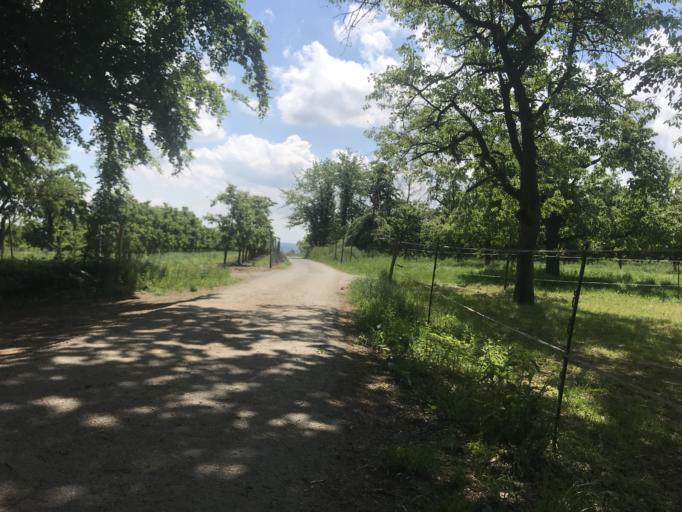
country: DE
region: Hesse
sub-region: Regierungsbezirk Darmstadt
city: Walluf
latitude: 50.0715
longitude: 8.1570
